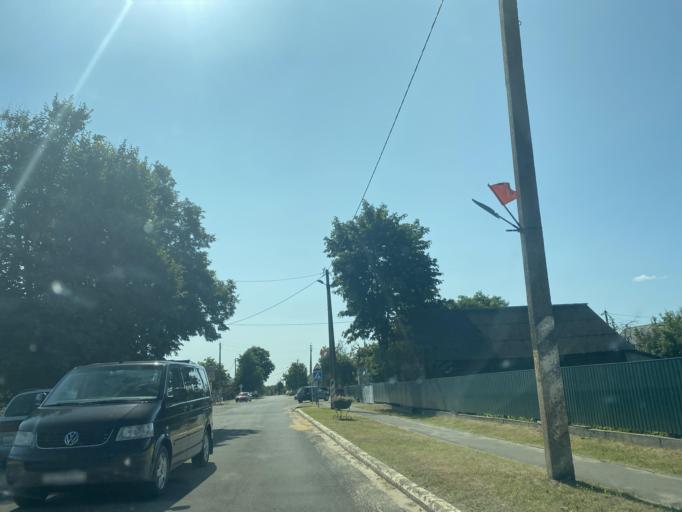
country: BY
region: Brest
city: Ivanava
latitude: 52.3155
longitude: 25.6119
